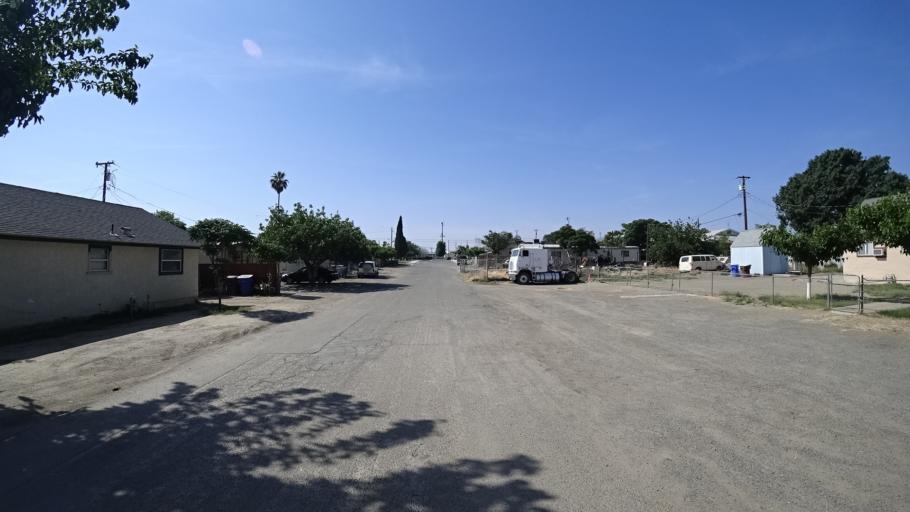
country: US
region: California
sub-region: Kings County
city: Kettleman City
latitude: 36.0101
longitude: -119.9625
